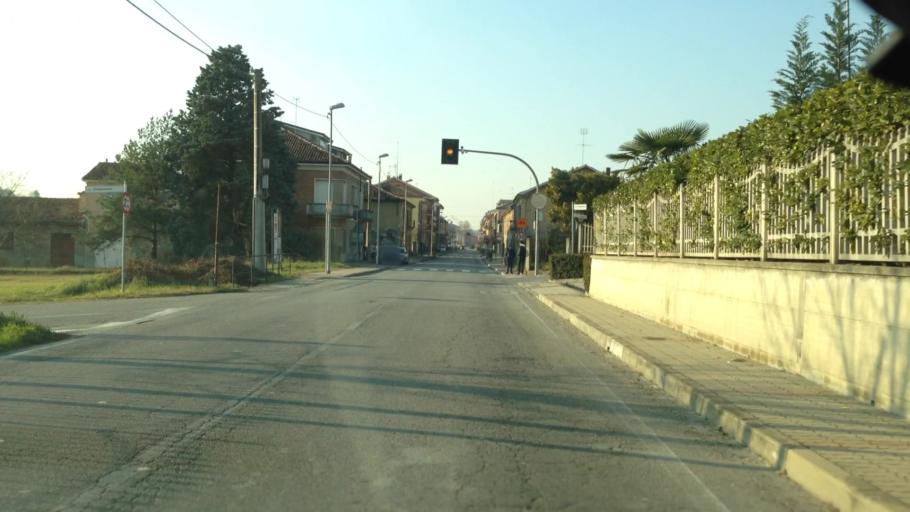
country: IT
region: Piedmont
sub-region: Provincia di Asti
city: Montegrosso
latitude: 44.8180
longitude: 8.2450
